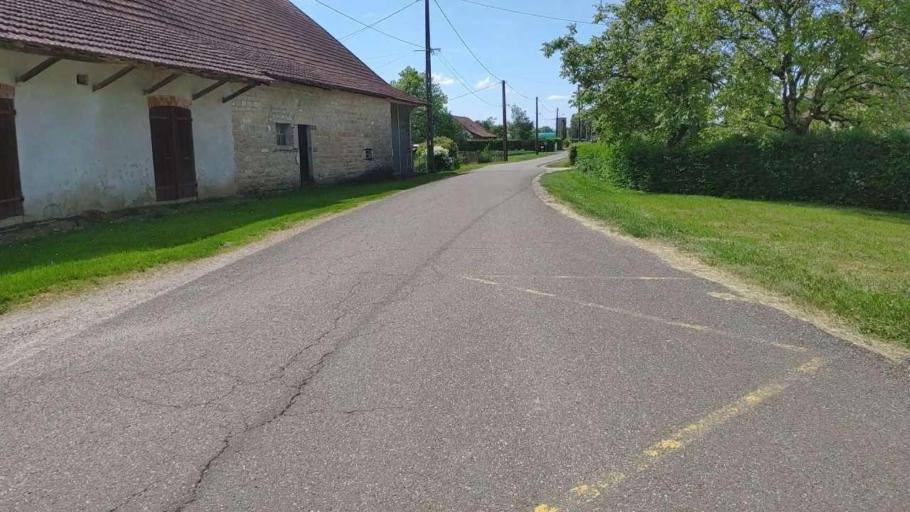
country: FR
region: Franche-Comte
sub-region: Departement du Jura
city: Bletterans
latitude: 46.7056
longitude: 5.4116
